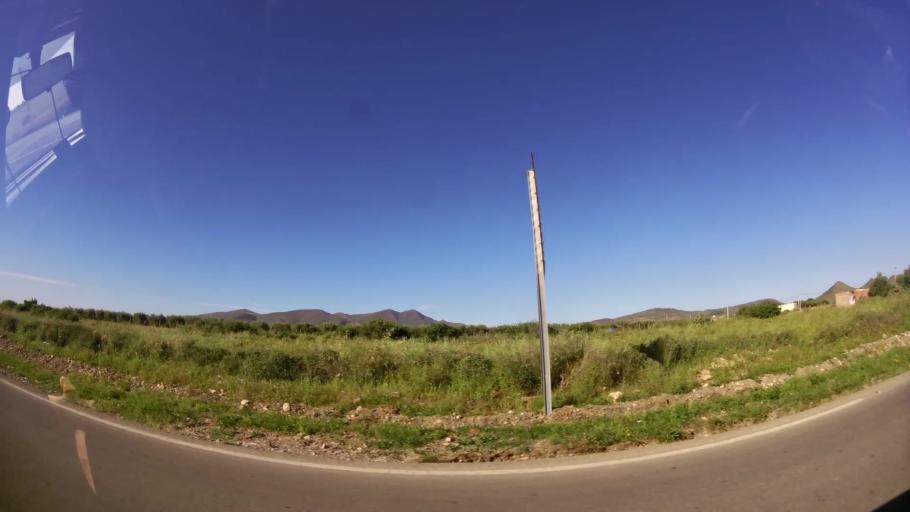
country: MA
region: Oriental
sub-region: Berkane-Taourirt
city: Ahfir
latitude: 34.9666
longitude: -2.1172
